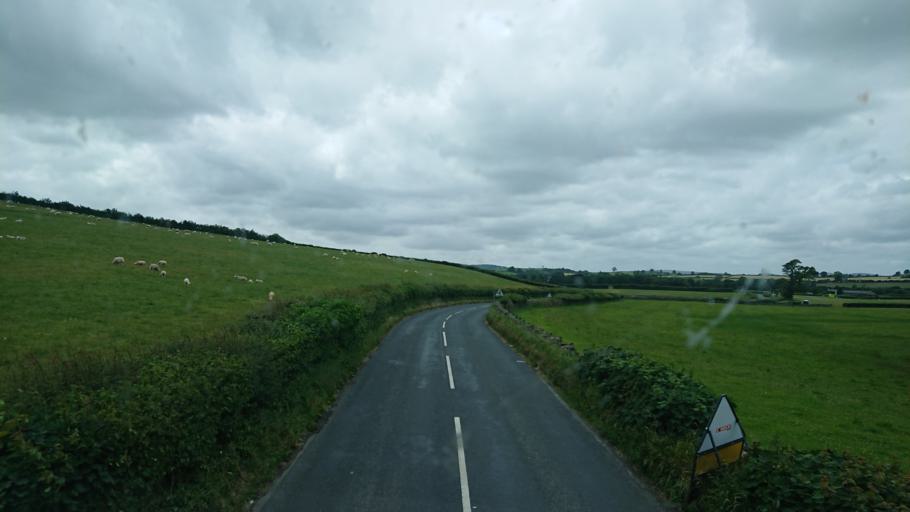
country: GB
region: England
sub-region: Cumbria
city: Milnthorpe
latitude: 54.2461
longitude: -2.7188
